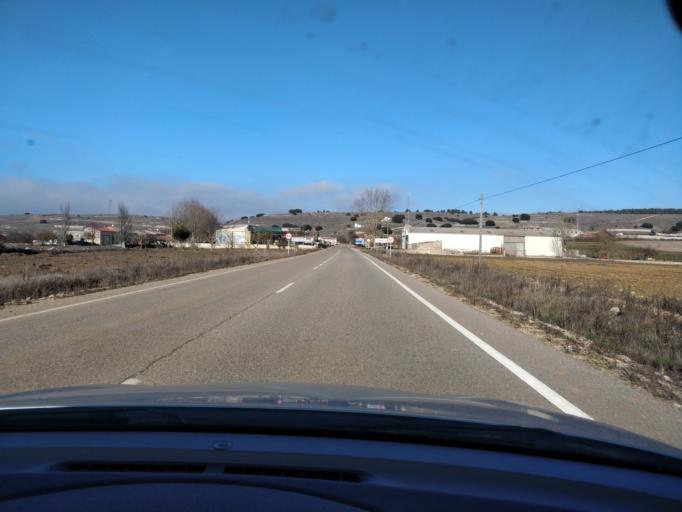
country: ES
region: Castille and Leon
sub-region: Provincia de Burgos
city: Abajas
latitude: 42.6353
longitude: -3.6240
